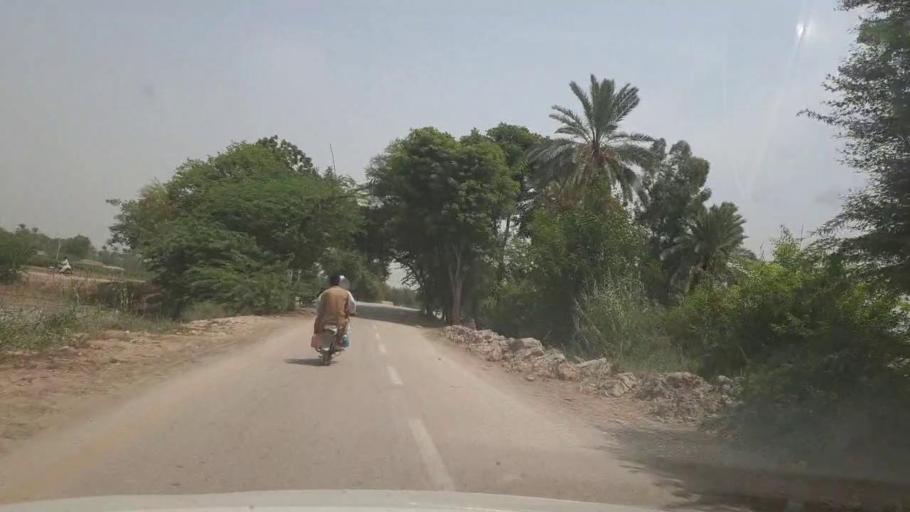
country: PK
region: Sindh
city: Kot Diji
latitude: 27.3856
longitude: 68.6549
